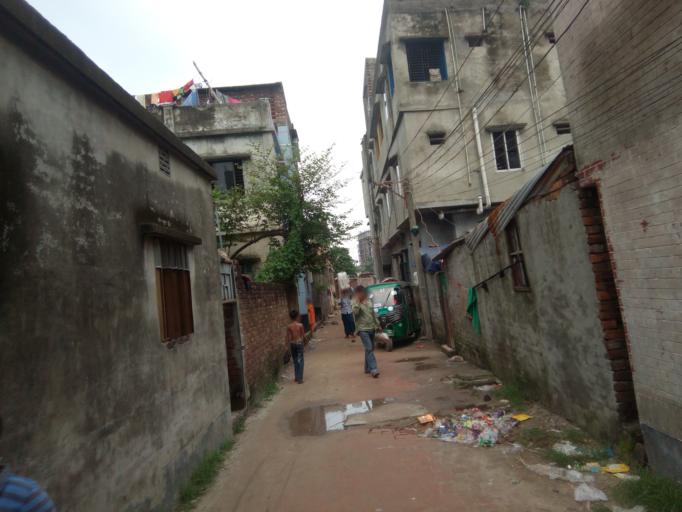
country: BD
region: Dhaka
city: Azimpur
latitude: 23.7341
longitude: 90.3574
